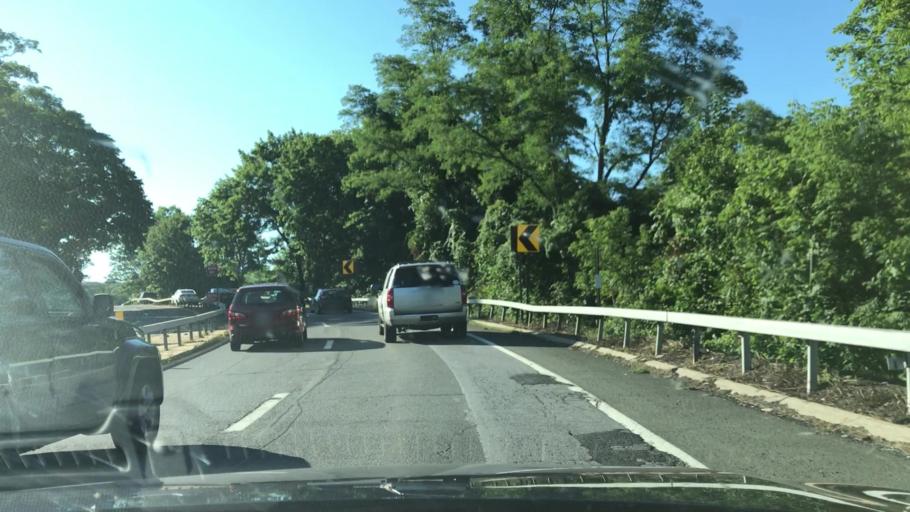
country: US
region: New York
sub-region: Westchester County
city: Hawthorne
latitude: 41.0966
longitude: -73.7933
